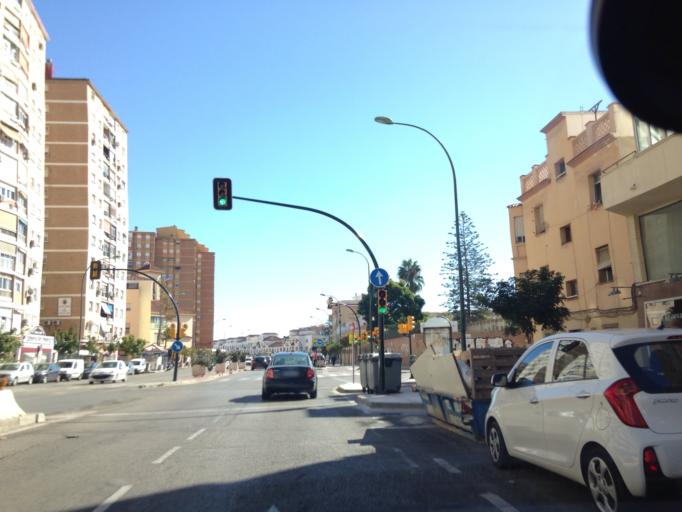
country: ES
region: Andalusia
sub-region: Provincia de Malaga
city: Malaga
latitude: 36.7032
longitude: -4.4403
